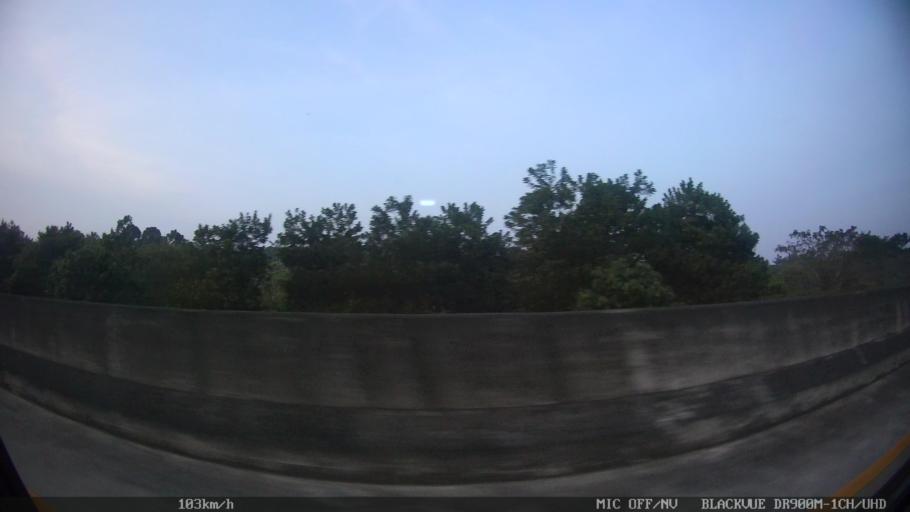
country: ID
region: Lampung
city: Kalianda
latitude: -5.7033
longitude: 105.6364
